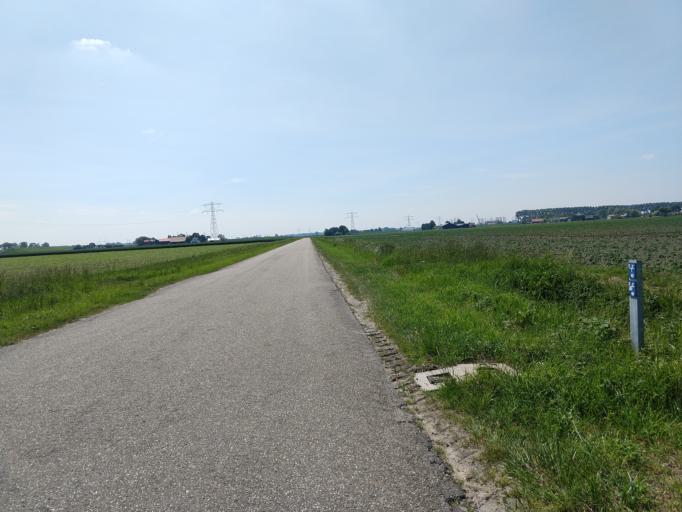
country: NL
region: Zeeland
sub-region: Gemeente Borsele
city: Borssele
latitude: 51.4863
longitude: 3.7884
